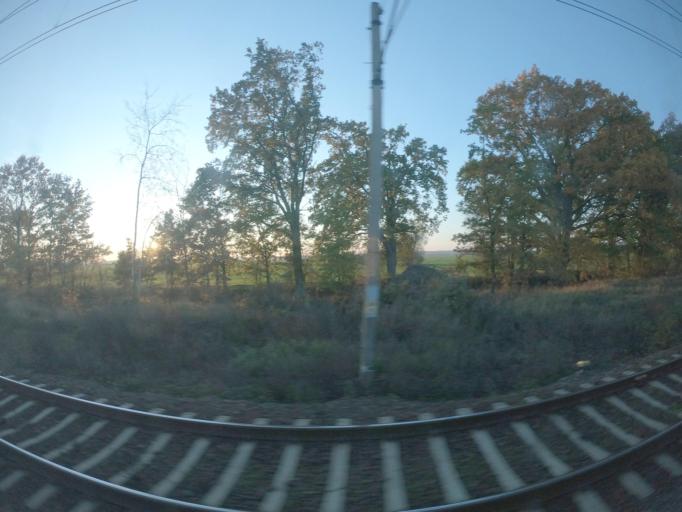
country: PL
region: Lubusz
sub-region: Powiat slubicki
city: Gorzyca
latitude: 52.5265
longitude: 14.6505
